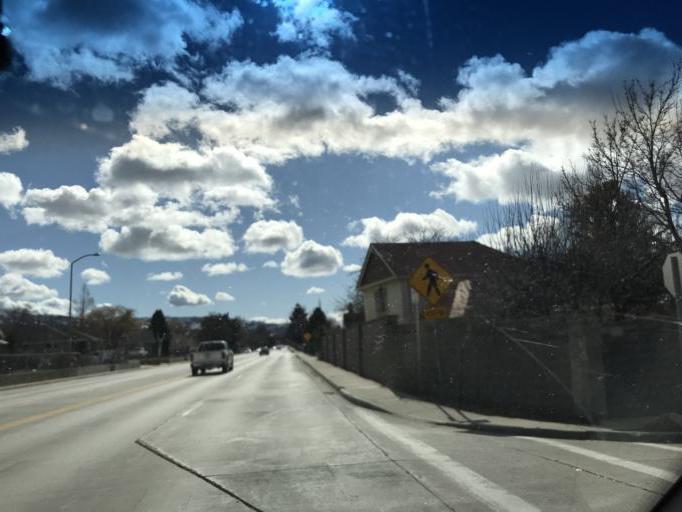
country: US
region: Utah
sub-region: Davis County
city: Bountiful
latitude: 40.8785
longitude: -111.8735
